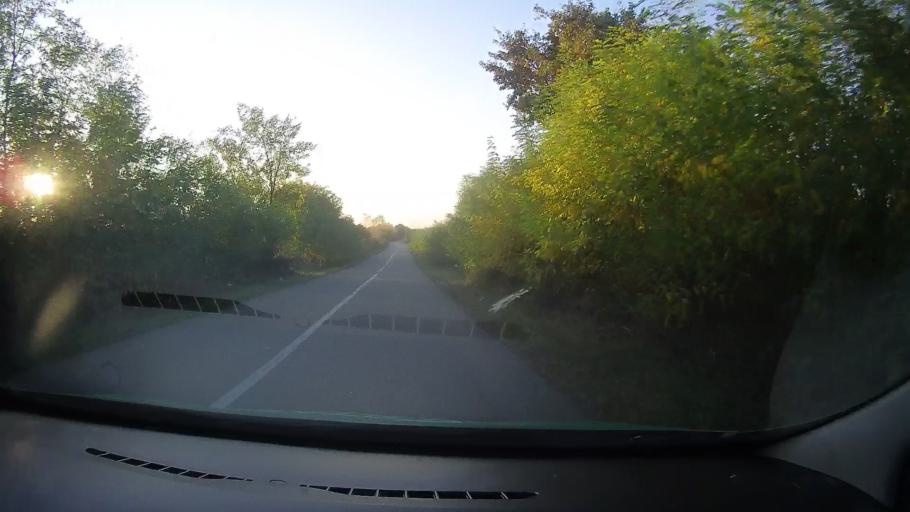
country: RO
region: Timis
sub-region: Comuna Traian Vuia
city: Traian Vuia
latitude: 45.7835
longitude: 22.0457
